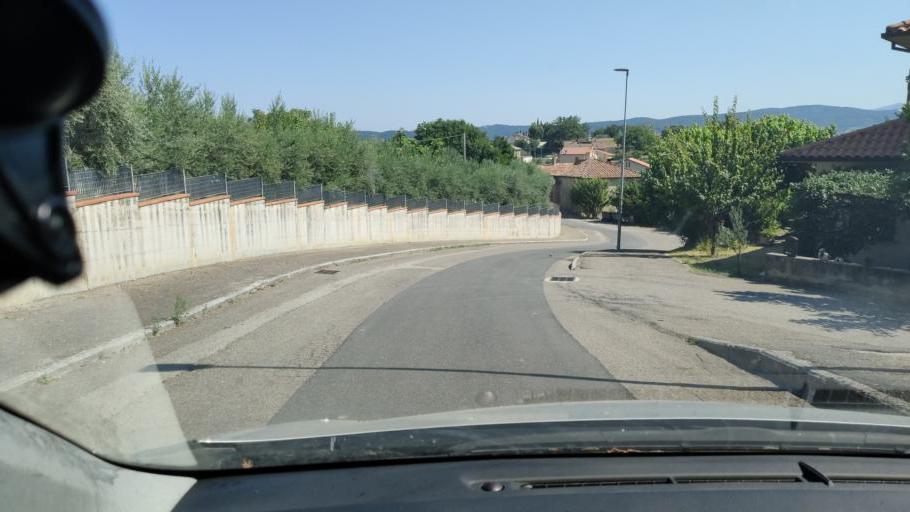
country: IT
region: Umbria
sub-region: Provincia di Terni
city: Fornole
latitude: 42.5155
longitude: 12.4308
